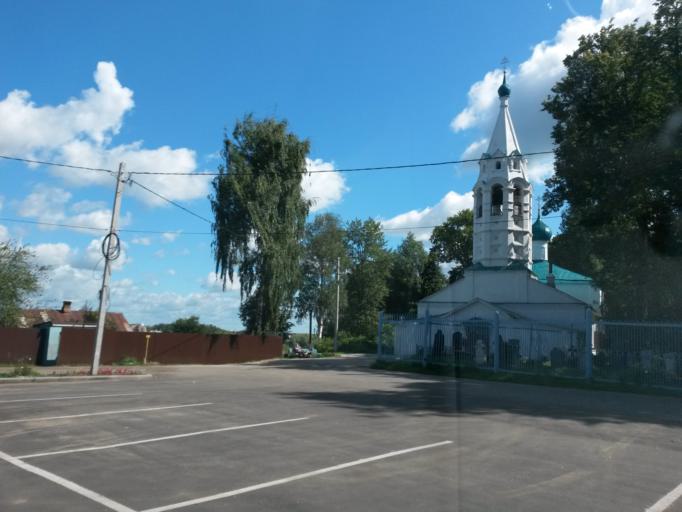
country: RU
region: Jaroslavl
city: Yaroslavl
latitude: 57.6047
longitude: 39.8910
